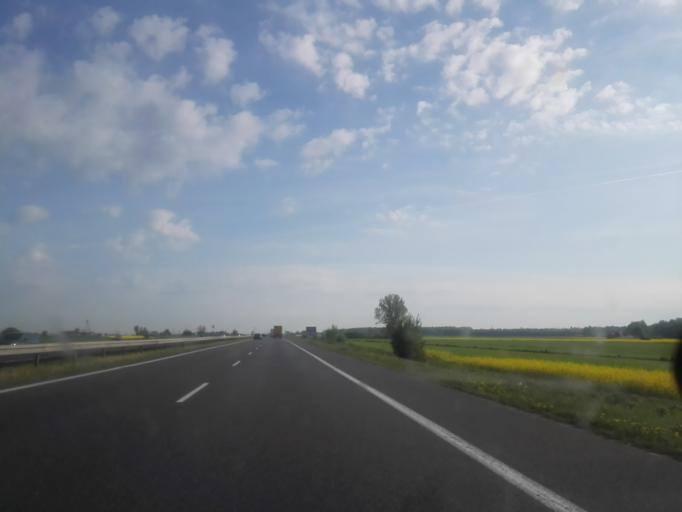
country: PL
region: Lodz Voivodeship
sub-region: Powiat piotrkowski
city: Wola Krzysztoporska
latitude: 51.3802
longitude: 19.6238
